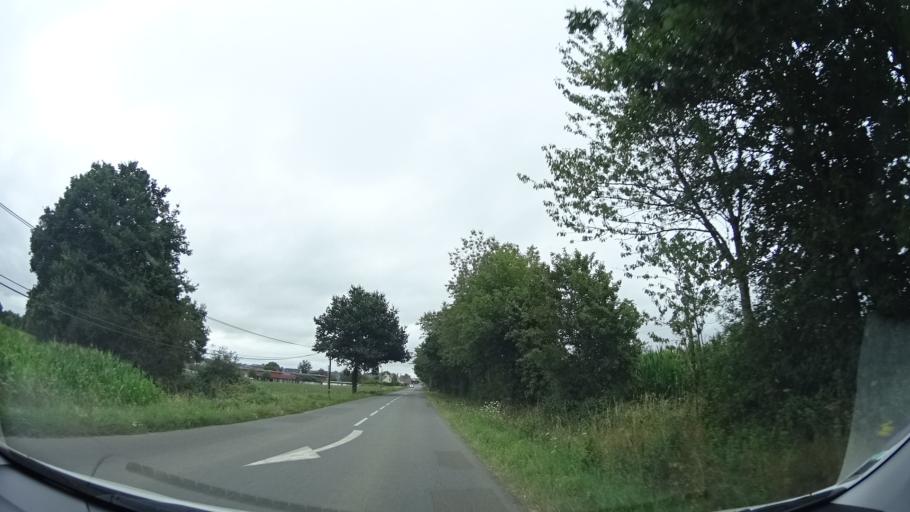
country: FR
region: Brittany
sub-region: Departement d'Ille-et-Vilaine
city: Saint-Domineuc
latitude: 48.3705
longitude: -1.8818
